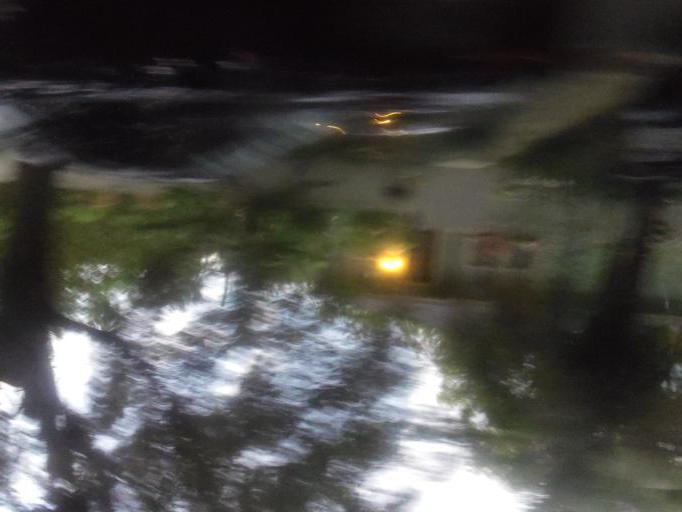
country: US
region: Florida
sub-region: Duval County
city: Jacksonville
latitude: 30.2969
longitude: -81.7126
